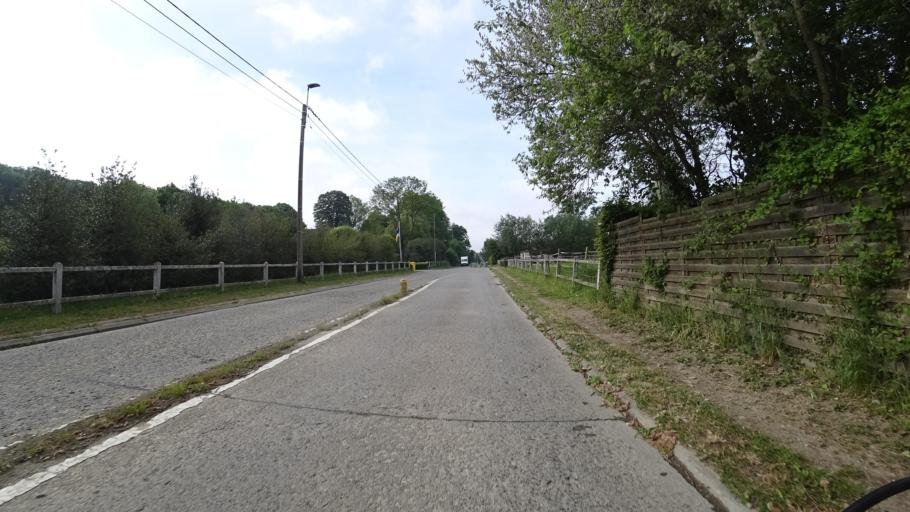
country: BE
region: Wallonia
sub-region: Province du Brabant Wallon
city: Grez-Doiceau
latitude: 50.7268
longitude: 4.6639
